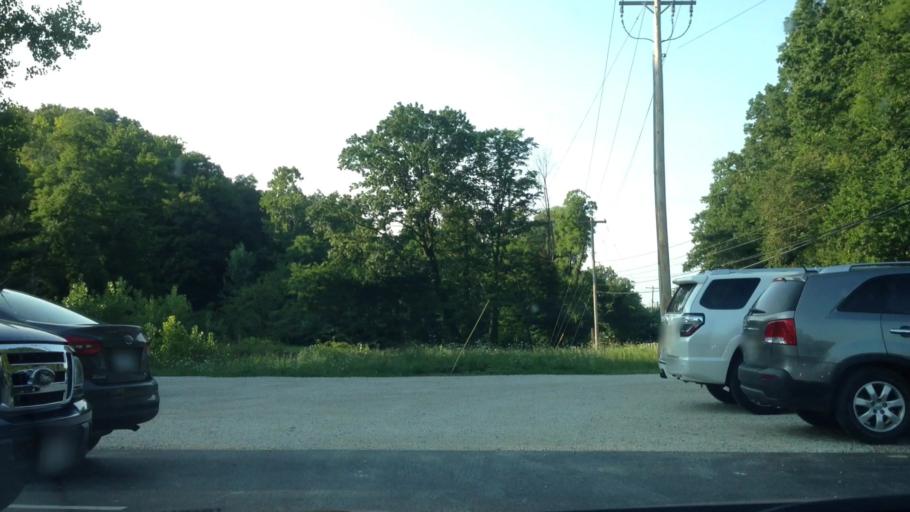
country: US
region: Ohio
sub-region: Summit County
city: Montrose-Ghent
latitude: 41.1594
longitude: -81.6374
